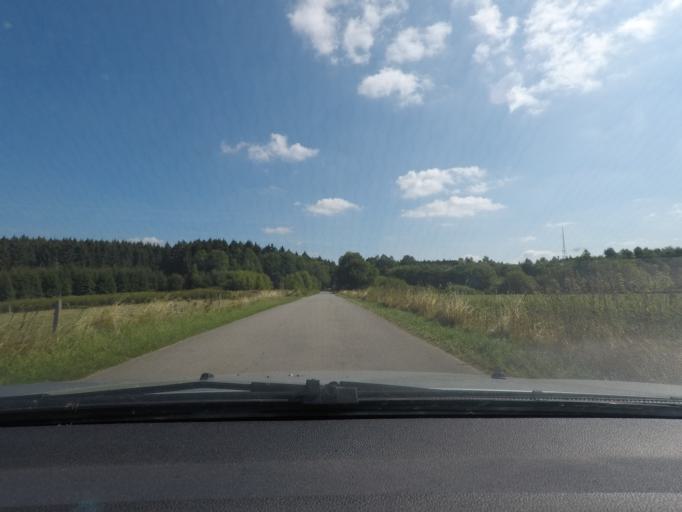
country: BE
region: Wallonia
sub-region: Province du Luxembourg
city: Fauvillers
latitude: 49.7998
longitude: 5.6327
